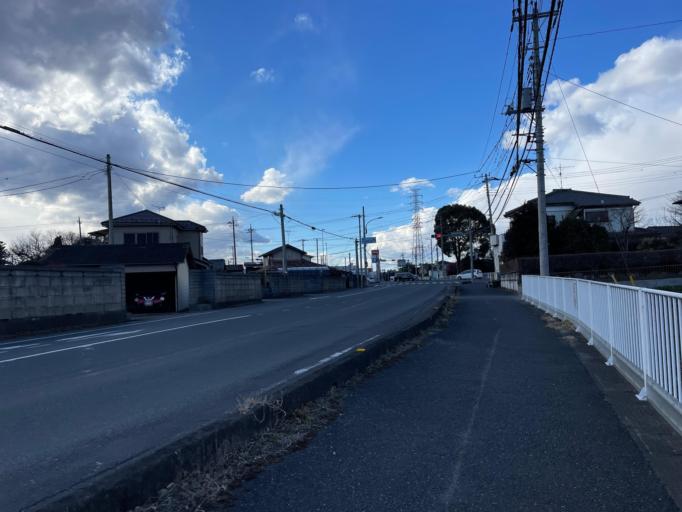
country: JP
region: Saitama
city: Ogawa
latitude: 36.0378
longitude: 139.3364
